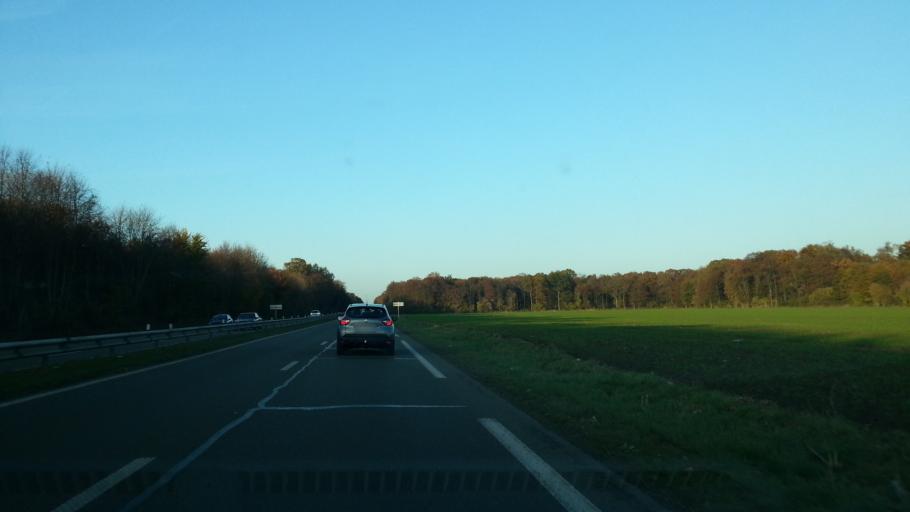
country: FR
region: Picardie
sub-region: Departement de l'Oise
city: Saint-Maximin
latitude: 49.2147
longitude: 2.4652
